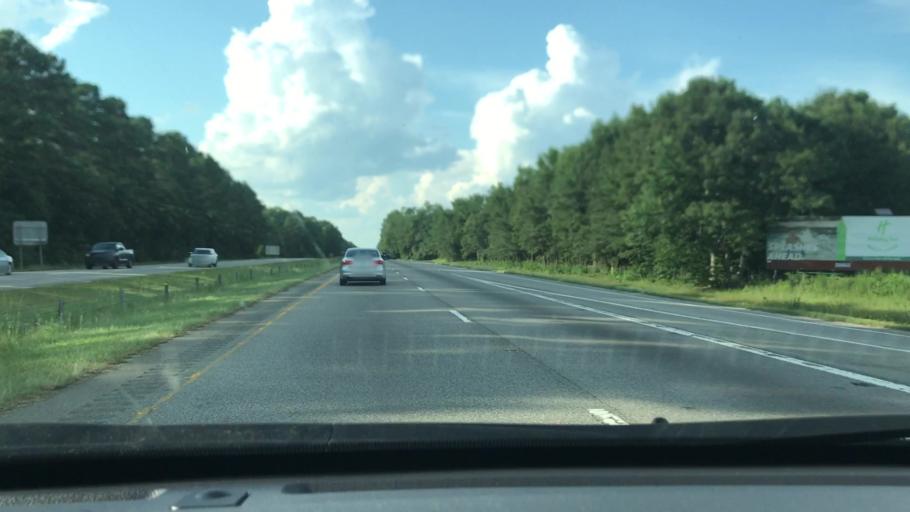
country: US
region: North Carolina
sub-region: Robeson County
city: Saint Pauls
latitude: 34.7233
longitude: -78.9973
